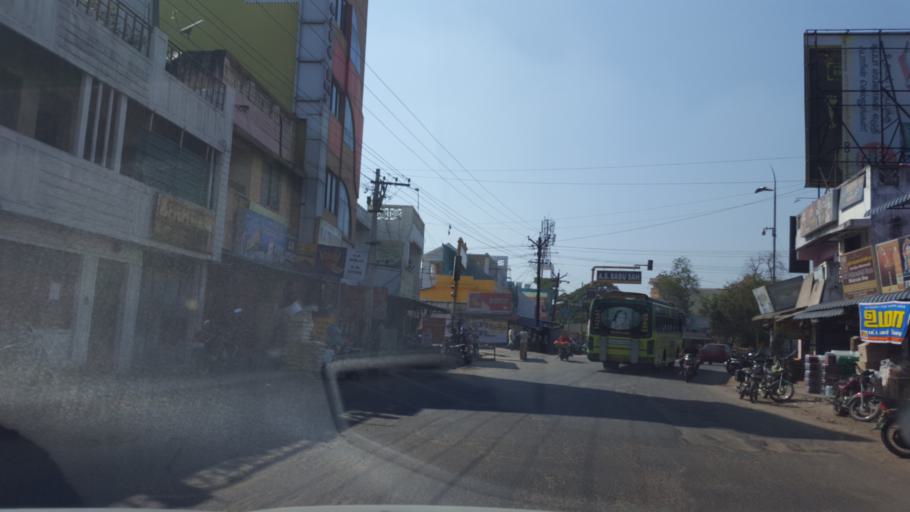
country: IN
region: Tamil Nadu
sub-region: Kancheepuram
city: Kanchipuram
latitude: 12.8448
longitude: 79.6971
